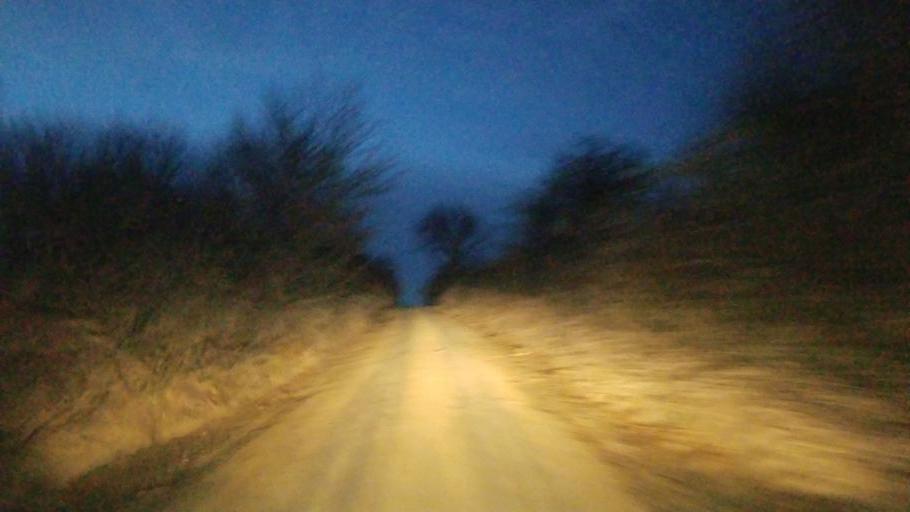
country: US
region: Nebraska
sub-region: Knox County
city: Center
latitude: 42.5742
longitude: -97.7985
